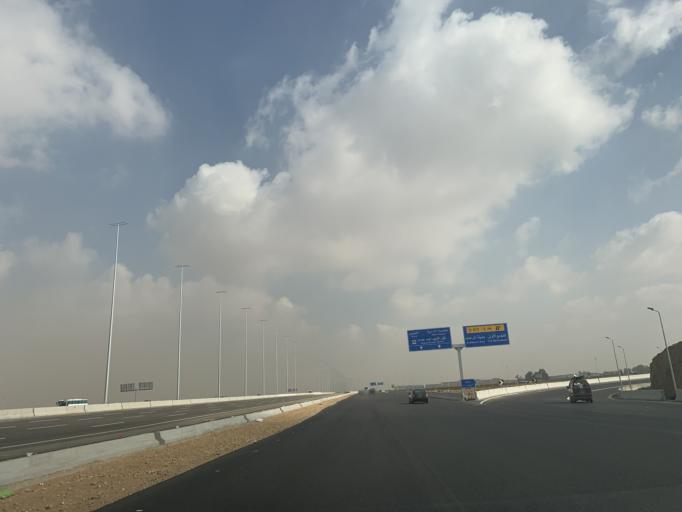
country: EG
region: Muhafazat al Qalyubiyah
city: Al Khankah
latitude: 30.0828
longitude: 31.4514
